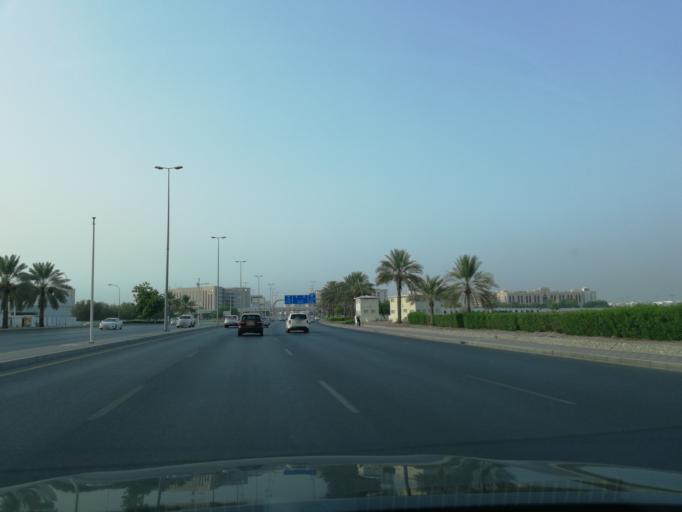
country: OM
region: Muhafazat Masqat
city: Bawshar
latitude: 23.5845
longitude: 58.3817
